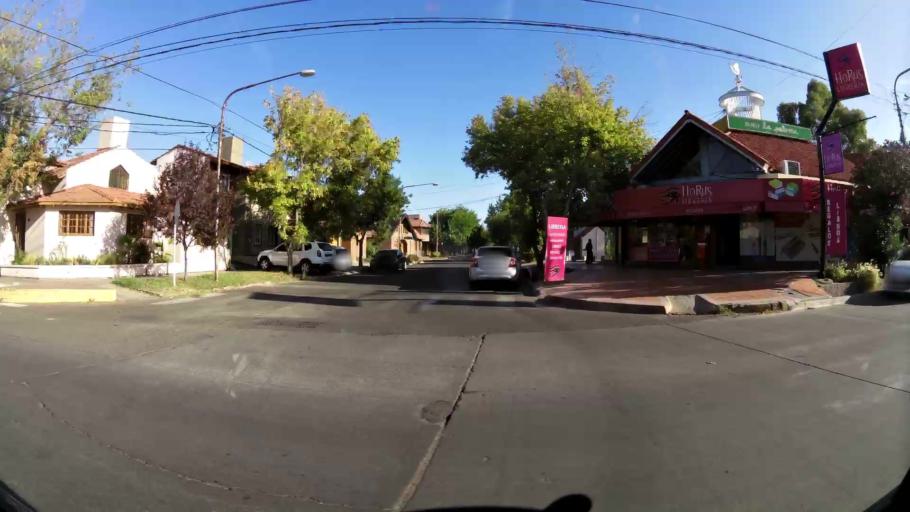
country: AR
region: Mendoza
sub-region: Departamento de Godoy Cruz
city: Godoy Cruz
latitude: -32.9127
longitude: -68.8372
